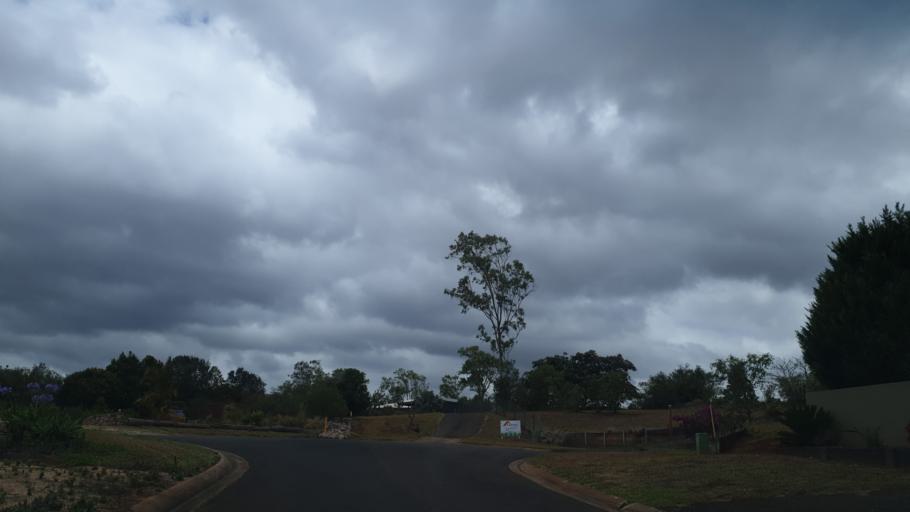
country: AU
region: Queensland
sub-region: Tablelands
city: Tolga
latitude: -17.2114
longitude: 145.4492
